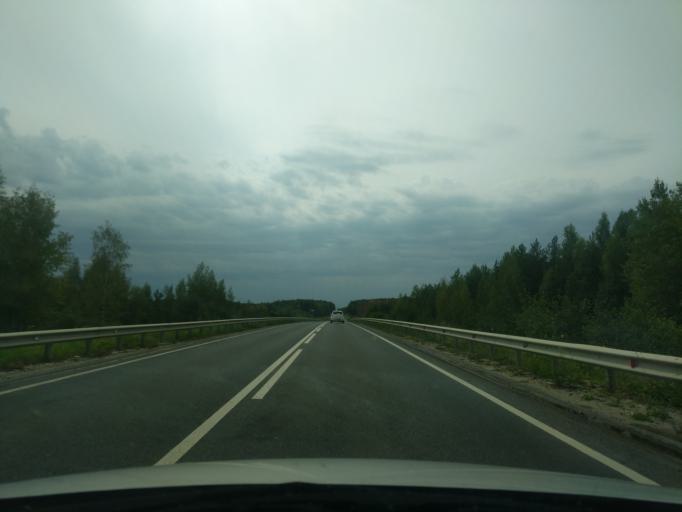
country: RU
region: Kostroma
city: Manturovo
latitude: 58.3290
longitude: 44.7167
